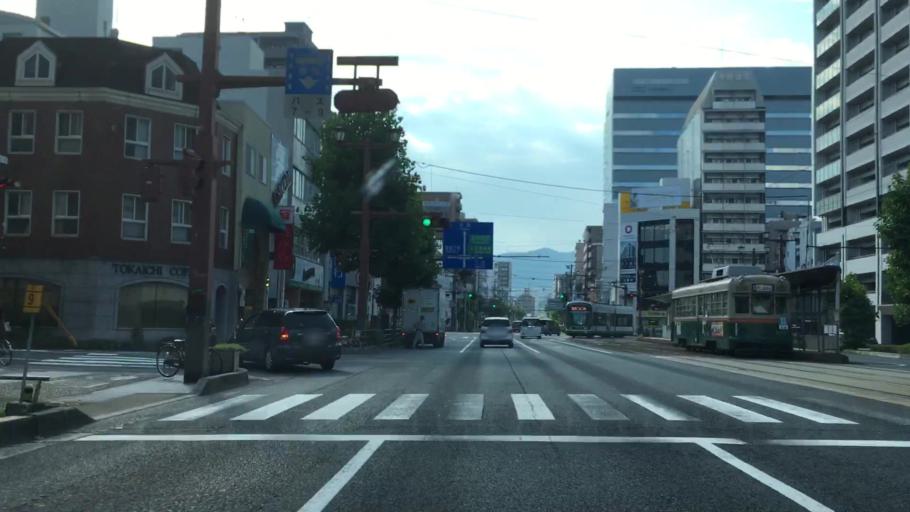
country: JP
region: Hiroshima
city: Hiroshima-shi
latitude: 34.3972
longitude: 132.4482
